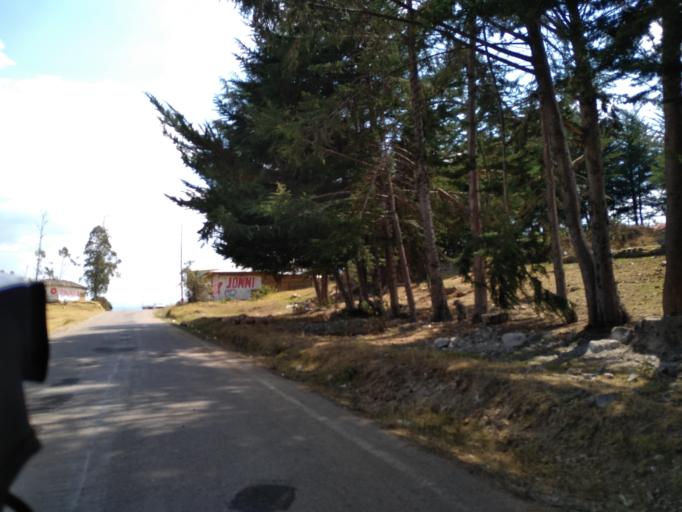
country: PE
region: Cajamarca
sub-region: Provincia de Celendin
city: Celendin
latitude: -6.8760
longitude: -78.1139
